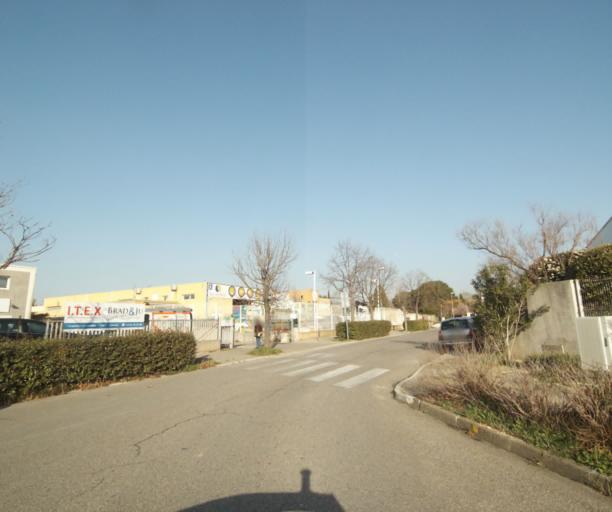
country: FR
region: Provence-Alpes-Cote d'Azur
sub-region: Departement des Bouches-du-Rhone
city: Les Pennes-Mirabeau
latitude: 43.4183
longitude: 5.2831
